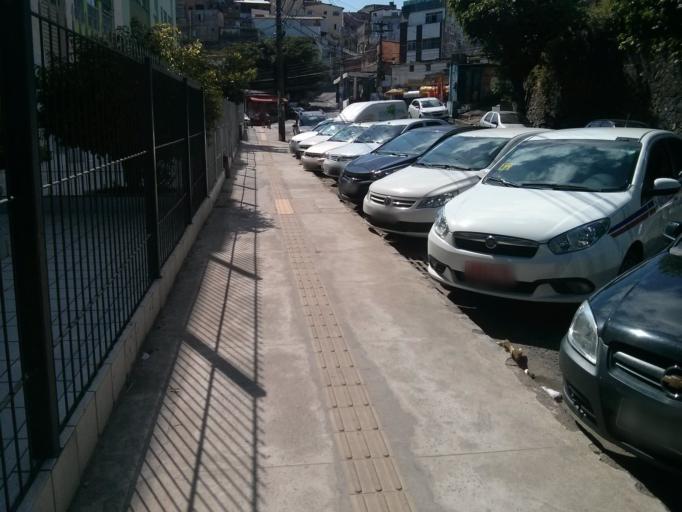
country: BR
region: Bahia
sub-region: Salvador
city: Salvador
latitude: -12.9955
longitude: -38.5042
